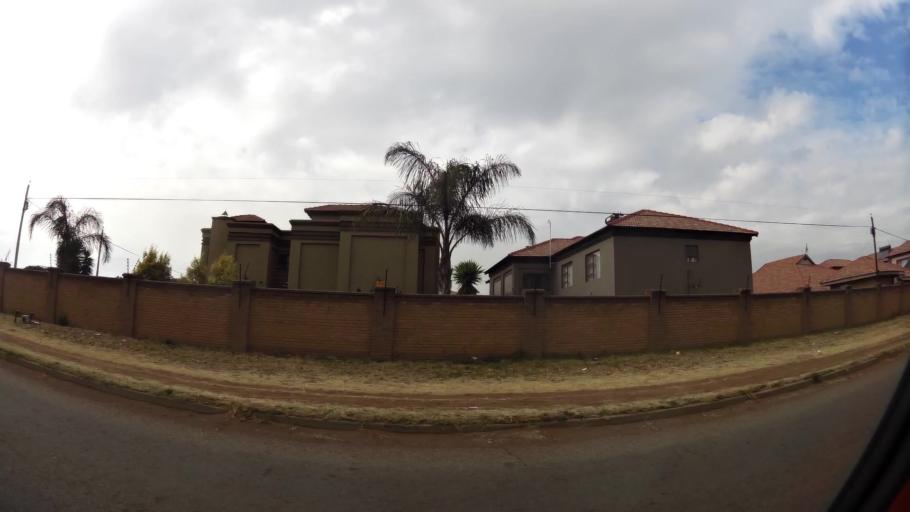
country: ZA
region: Gauteng
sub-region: Sedibeng District Municipality
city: Vanderbijlpark
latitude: -26.7232
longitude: 27.8627
